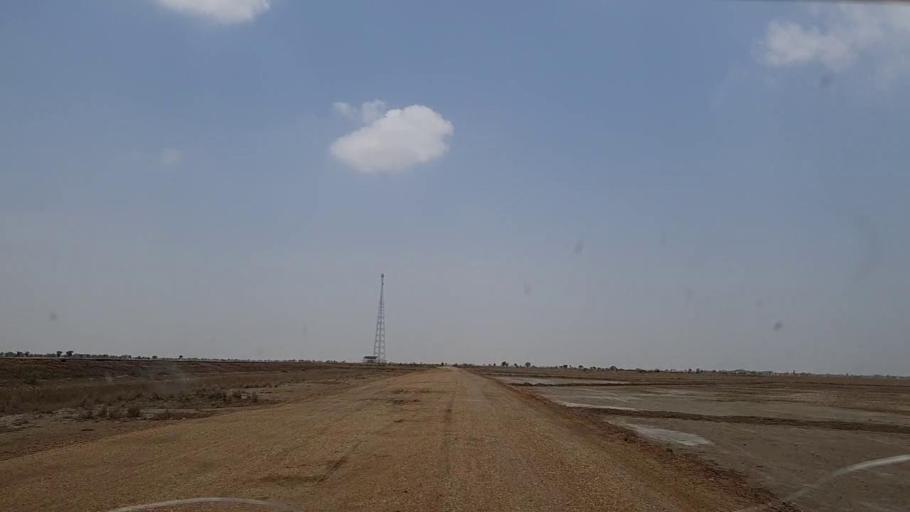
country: PK
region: Sindh
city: Johi
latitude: 26.7840
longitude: 67.6478
